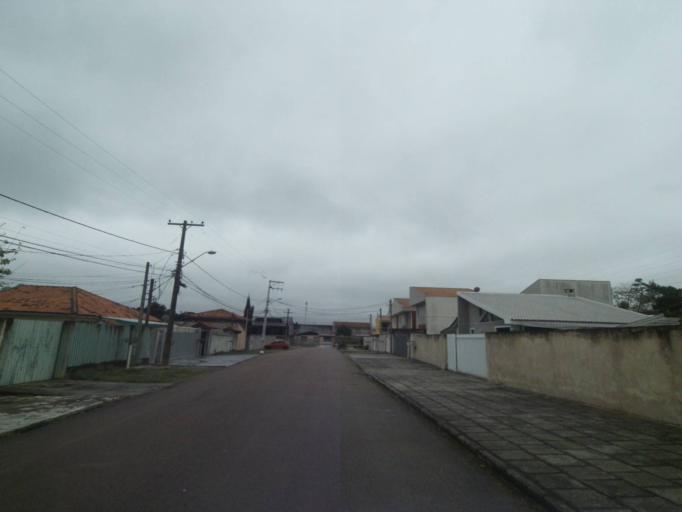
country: BR
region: Parana
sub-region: Curitiba
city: Curitiba
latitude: -25.5171
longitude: -49.3107
